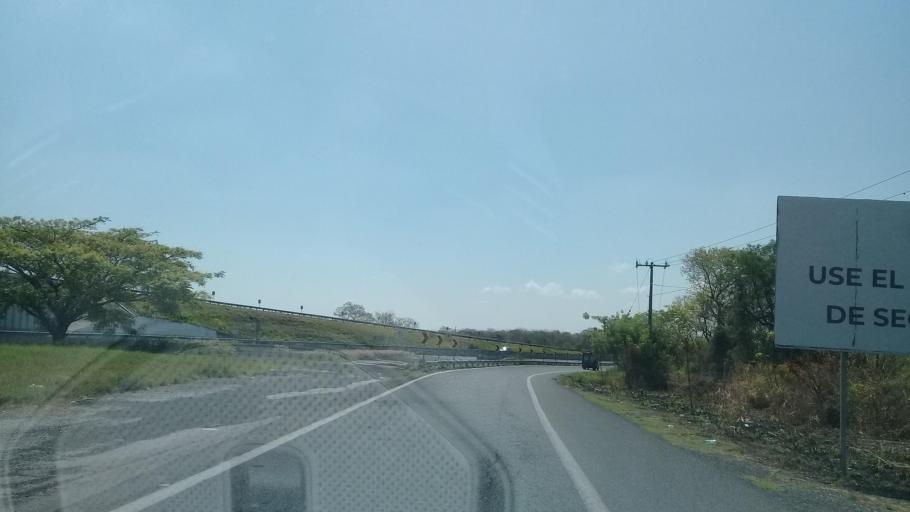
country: MX
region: Veracruz
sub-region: Emiliano Zapata
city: Plan del Rio
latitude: 19.3930
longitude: -96.6138
